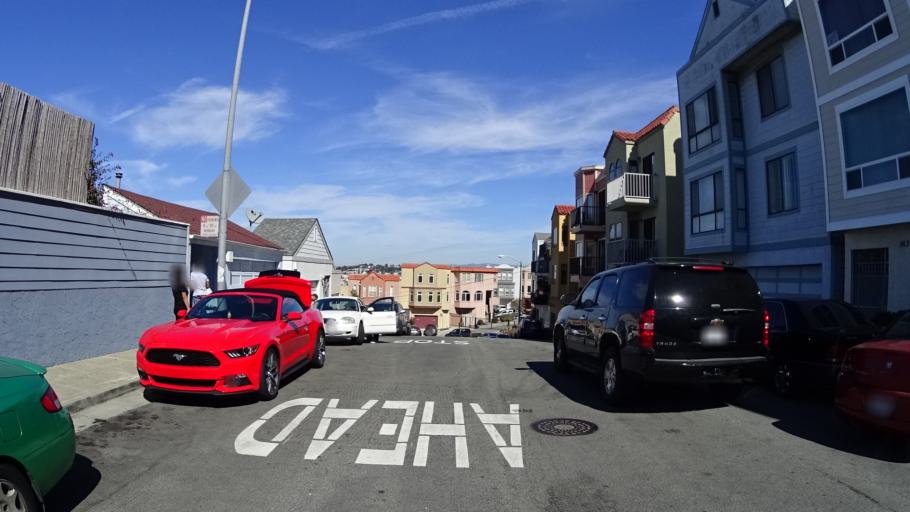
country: US
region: California
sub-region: San Mateo County
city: Brisbane
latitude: 37.7172
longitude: -122.3960
